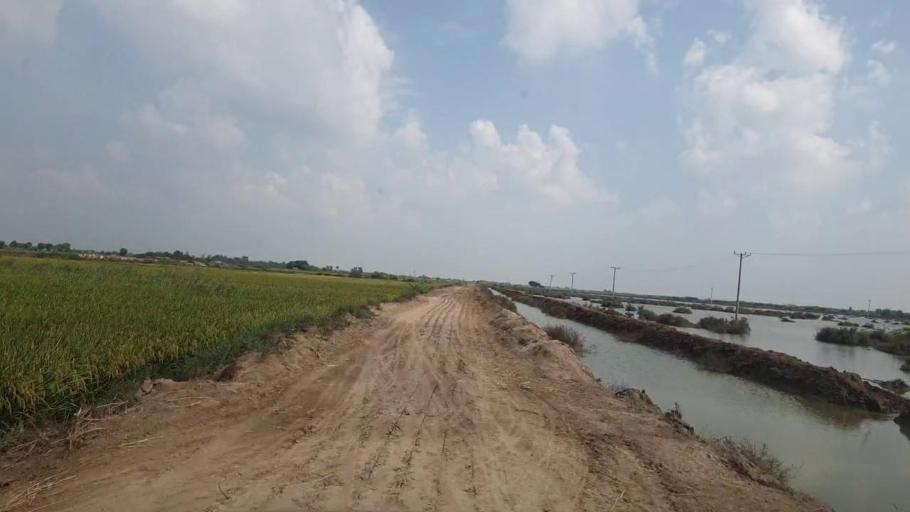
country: PK
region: Sindh
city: Badin
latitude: 24.5328
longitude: 68.6277
